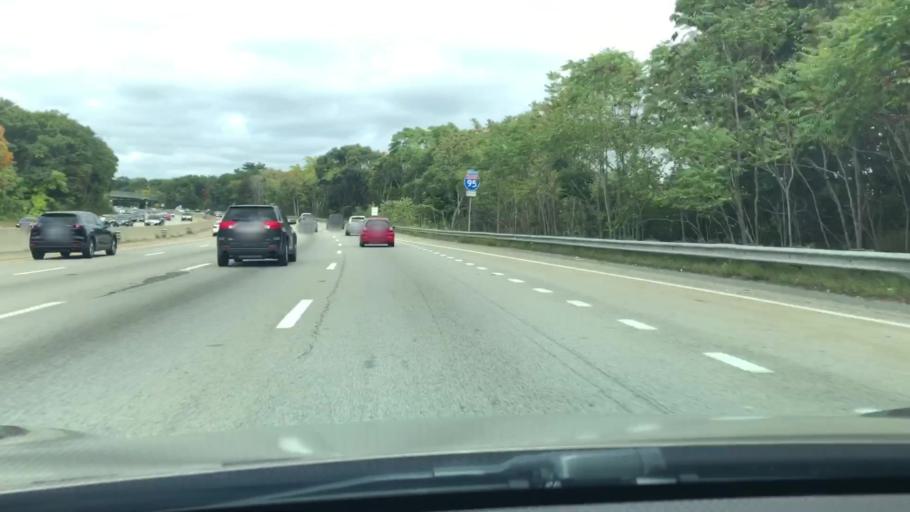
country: US
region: Massachusetts
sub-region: Middlesex County
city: Waltham
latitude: 42.3478
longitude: -71.2624
